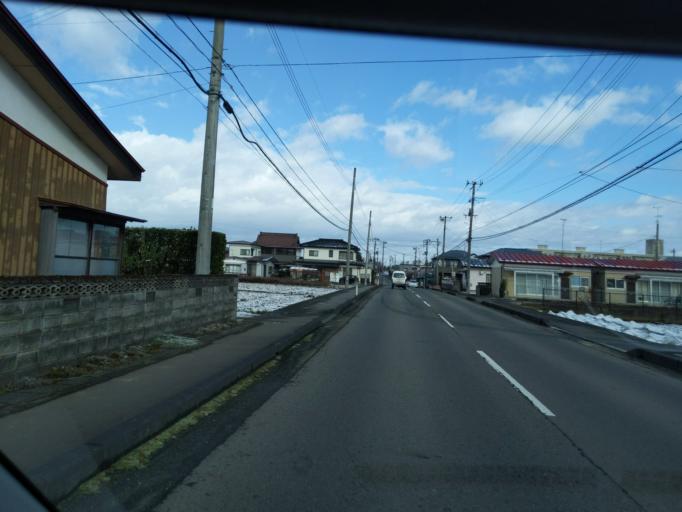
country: JP
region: Iwate
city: Mizusawa
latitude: 39.1141
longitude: 141.1374
